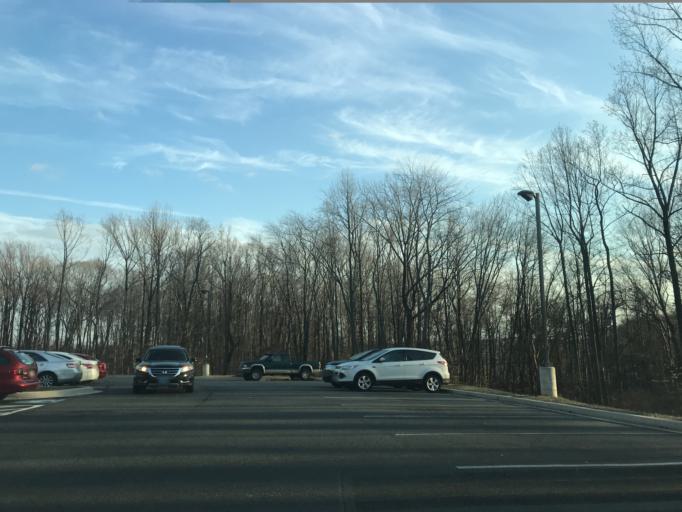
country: US
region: Maryland
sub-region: Harford County
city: Joppatowne
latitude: 39.4582
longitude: -76.3158
